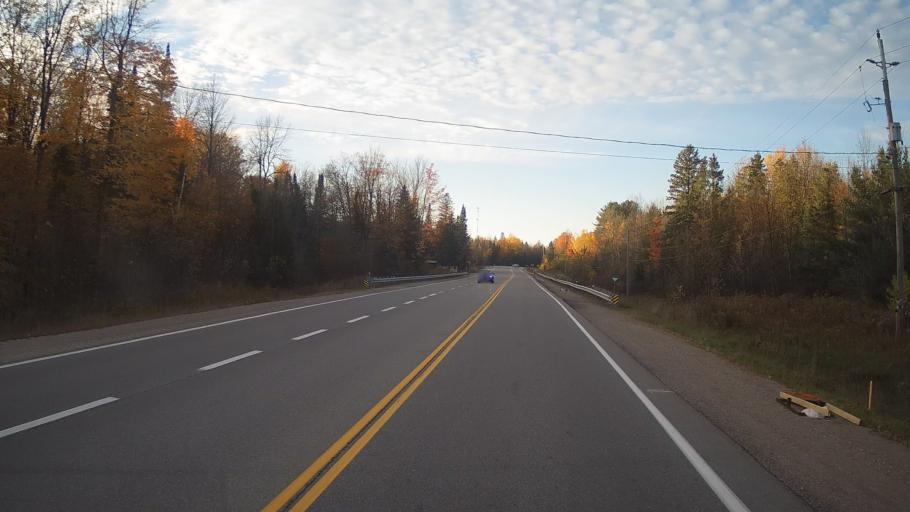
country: CA
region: Ontario
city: Perth
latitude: 45.0270
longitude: -76.2406
